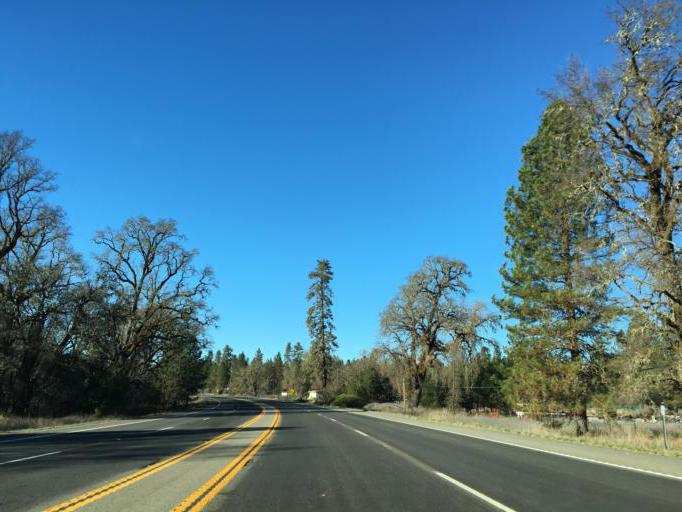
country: US
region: California
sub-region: Mendocino County
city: Laytonville
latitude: 39.7274
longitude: -123.5049
